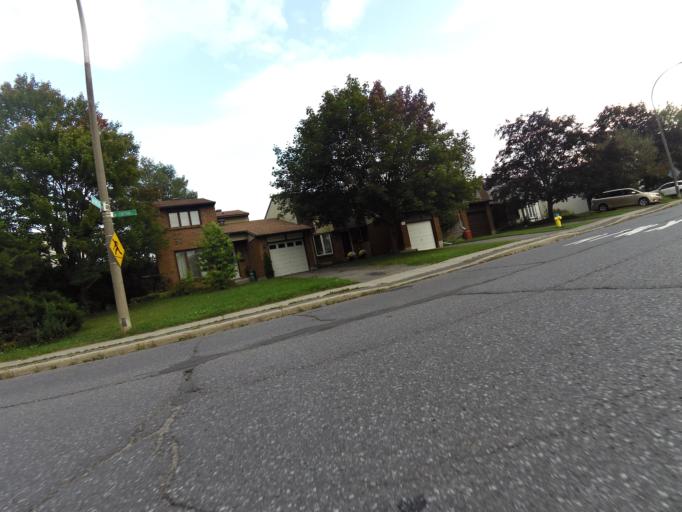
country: CA
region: Ontario
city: Bells Corners
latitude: 45.2715
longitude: -75.7533
